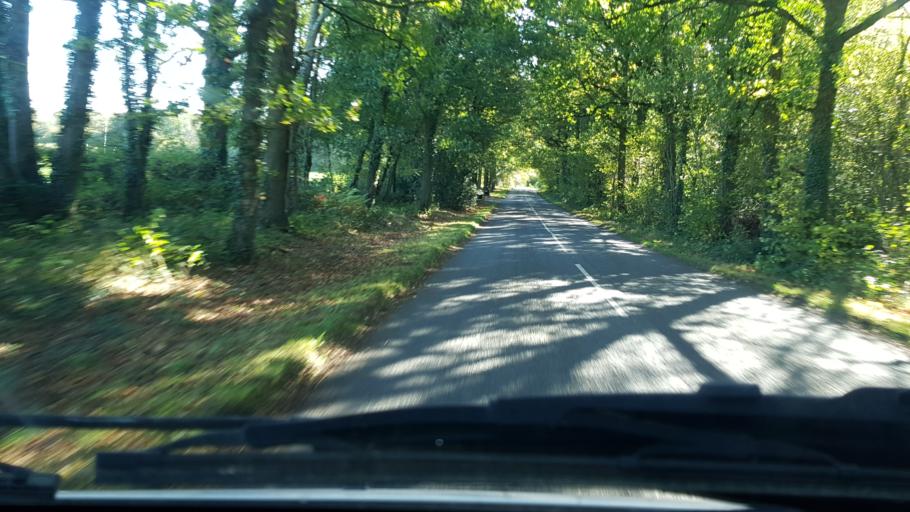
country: GB
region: England
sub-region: Surrey
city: Cranleigh
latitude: 51.1382
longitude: -0.4303
